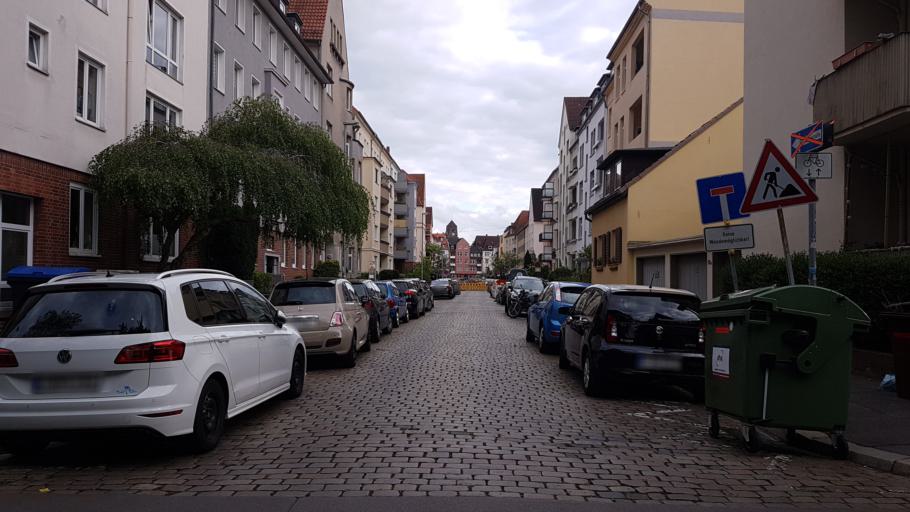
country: DE
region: Lower Saxony
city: Hannover
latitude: 52.3689
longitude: 9.7566
